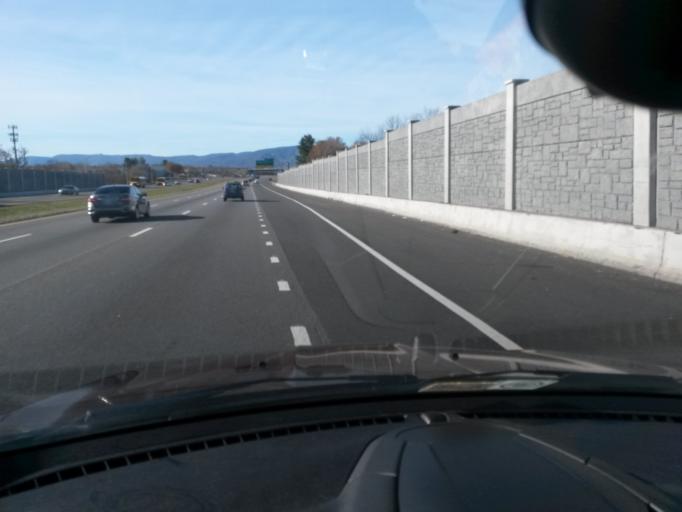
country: US
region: Virginia
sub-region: City of Roanoke
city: Roanoke
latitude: 37.2946
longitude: -79.9514
